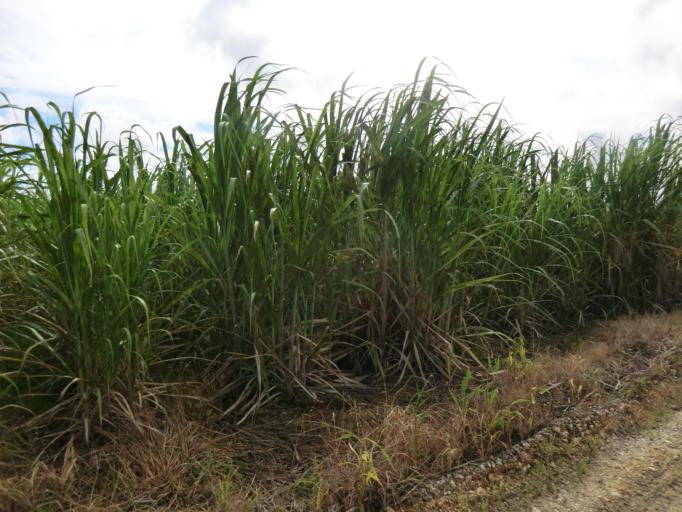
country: JP
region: Okinawa
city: Itoman
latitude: 26.1409
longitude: 127.7318
